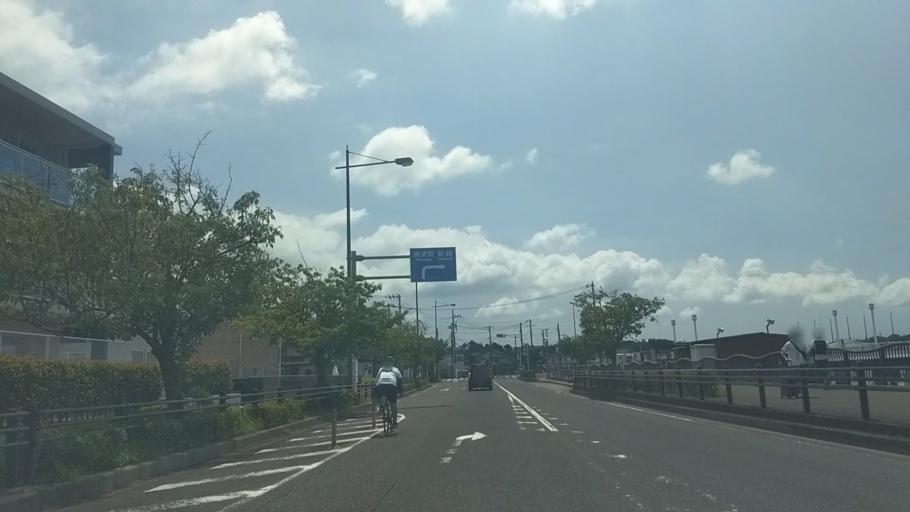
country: JP
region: Kanagawa
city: Yokosuka
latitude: 35.3271
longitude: 139.6311
